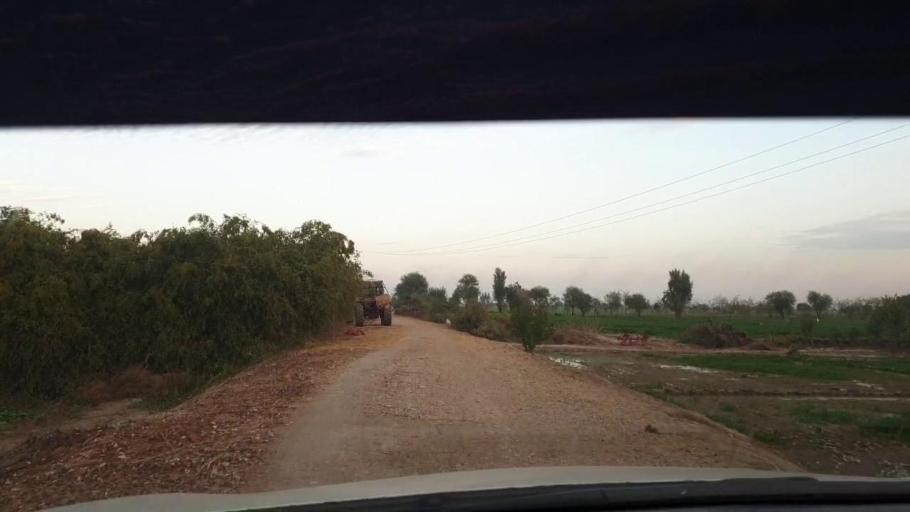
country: PK
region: Sindh
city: Berani
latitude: 25.8007
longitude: 68.8052
